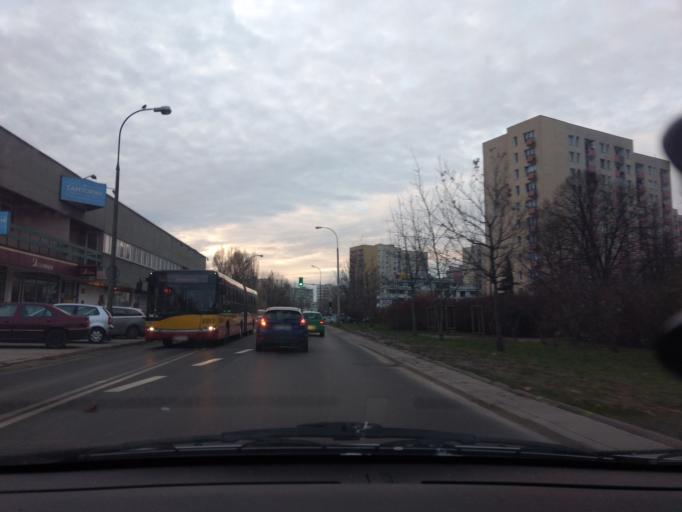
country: PL
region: Masovian Voivodeship
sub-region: Warszawa
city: Praga Poludnie
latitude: 52.2255
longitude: 21.0690
